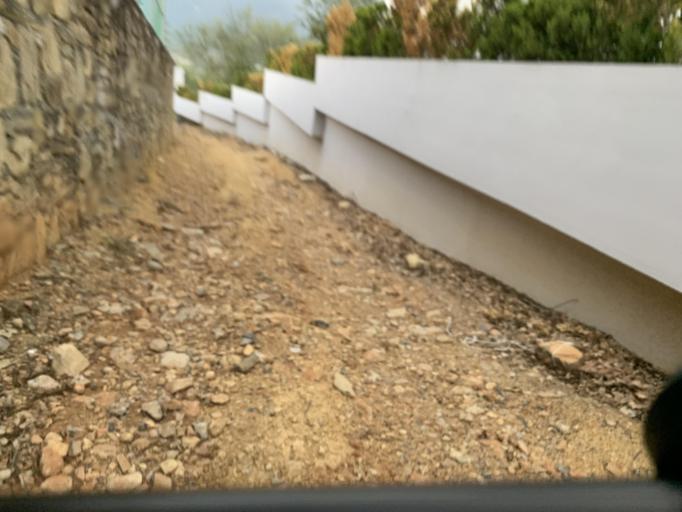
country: MX
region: Nuevo Leon
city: Santiago
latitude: 25.5058
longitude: -100.1781
